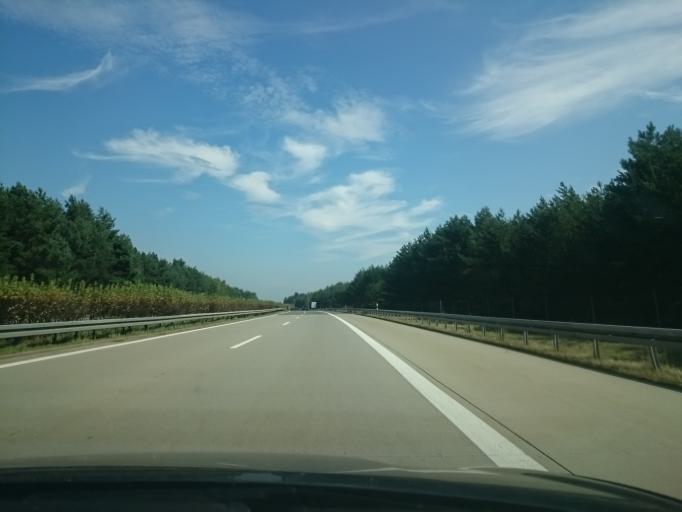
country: DE
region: Brandenburg
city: Ruhland
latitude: 51.4405
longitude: 13.8341
